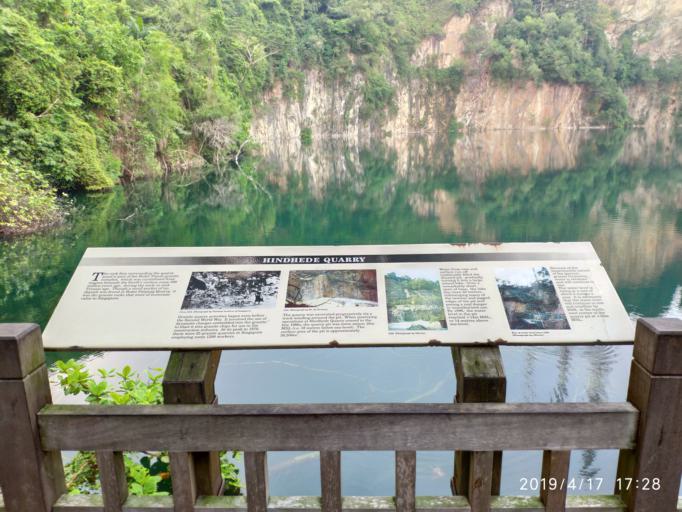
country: SG
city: Singapore
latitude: 1.3493
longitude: 103.7749
